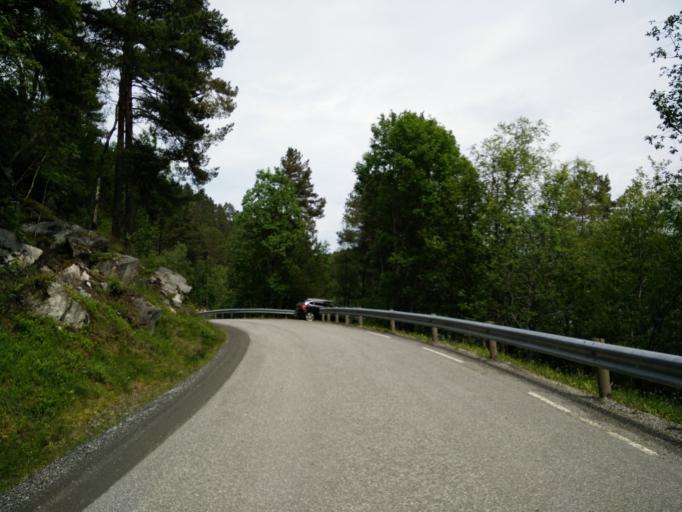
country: NO
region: More og Romsdal
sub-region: Kristiansund
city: Rensvik
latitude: 63.0254
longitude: 7.9531
